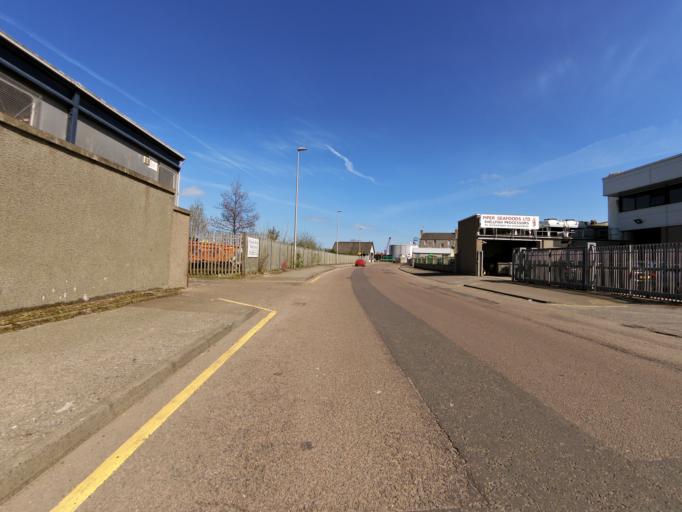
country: GB
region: Scotland
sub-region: Aberdeen City
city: Aberdeen
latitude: 57.1384
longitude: -2.0912
